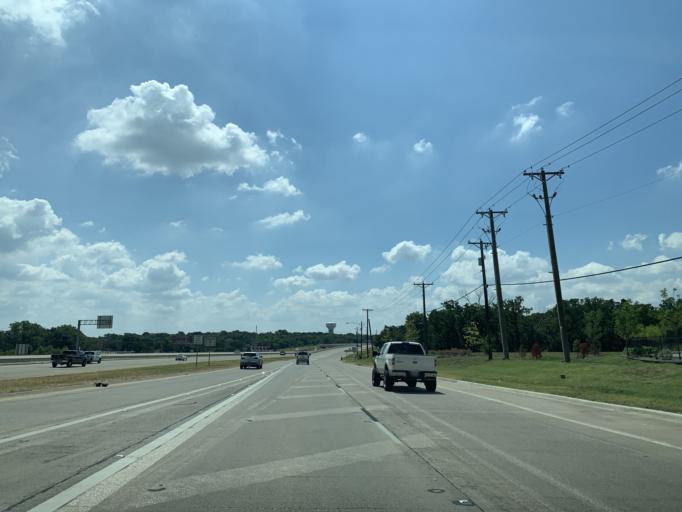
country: US
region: Texas
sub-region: Tarrant County
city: Azle
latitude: 32.8711
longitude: -97.5267
